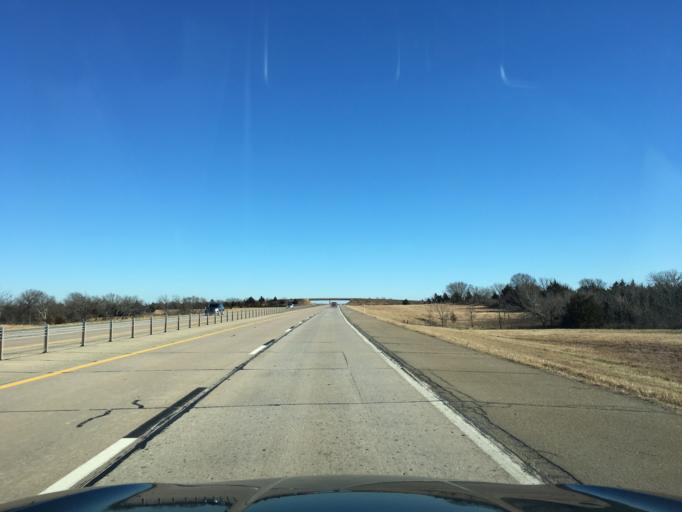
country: US
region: Oklahoma
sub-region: Pawnee County
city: Pawnee
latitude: 36.2254
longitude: -96.8798
